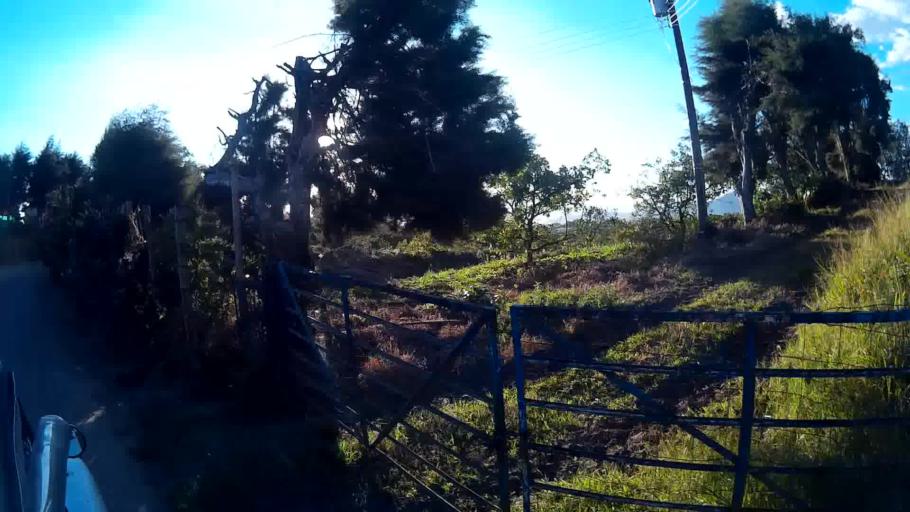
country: CO
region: Quindio
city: Filandia
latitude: 4.7335
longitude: -75.6789
